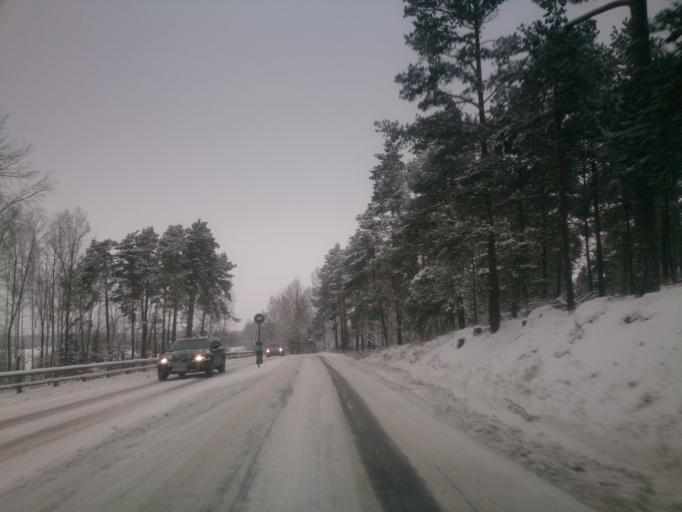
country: SE
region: OEstergoetland
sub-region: Norrkopings Kommun
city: Kimstad
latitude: 58.5559
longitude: 15.9537
